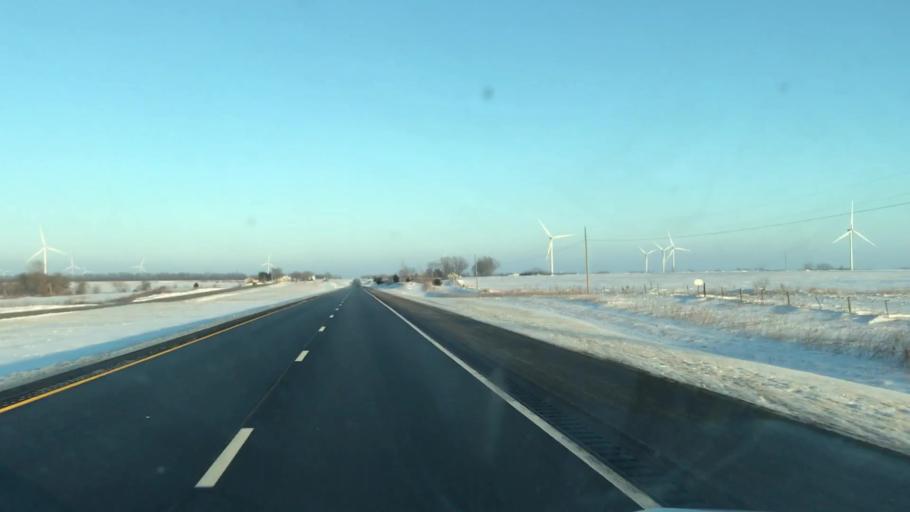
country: US
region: Missouri
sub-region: DeKalb County
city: Maysville
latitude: 39.7616
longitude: -94.4290
